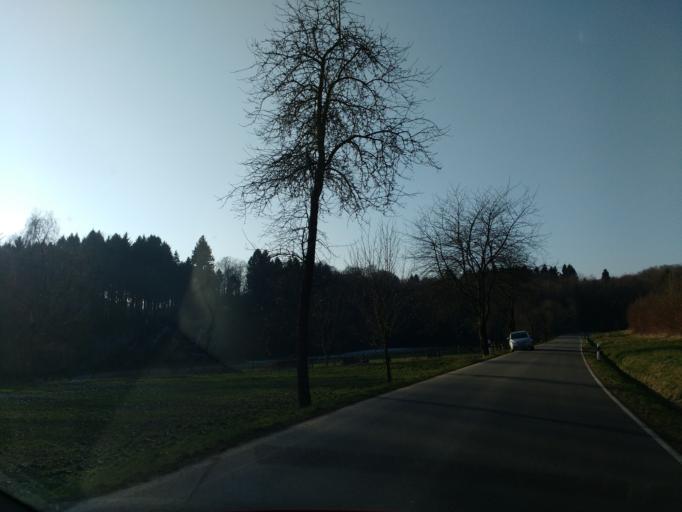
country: DE
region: North Rhine-Westphalia
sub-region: Regierungsbezirk Detmold
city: Bad Meinberg
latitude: 51.9041
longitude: 9.0388
